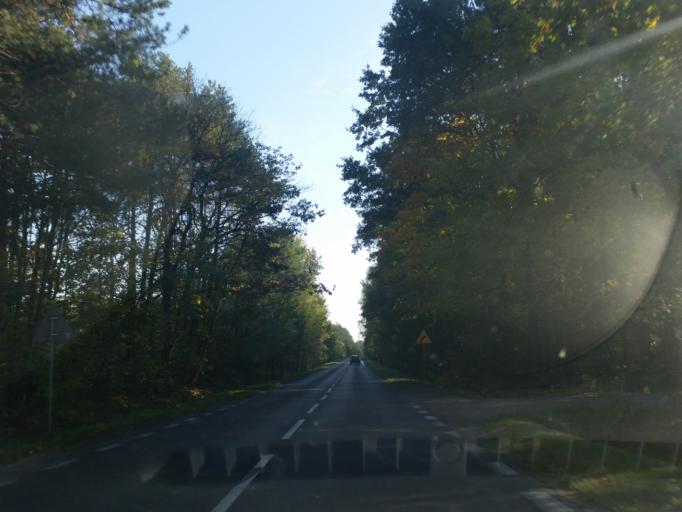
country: PL
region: Masovian Voivodeship
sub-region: Powiat sierpecki
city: Sierpc
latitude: 52.8945
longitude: 19.6503
